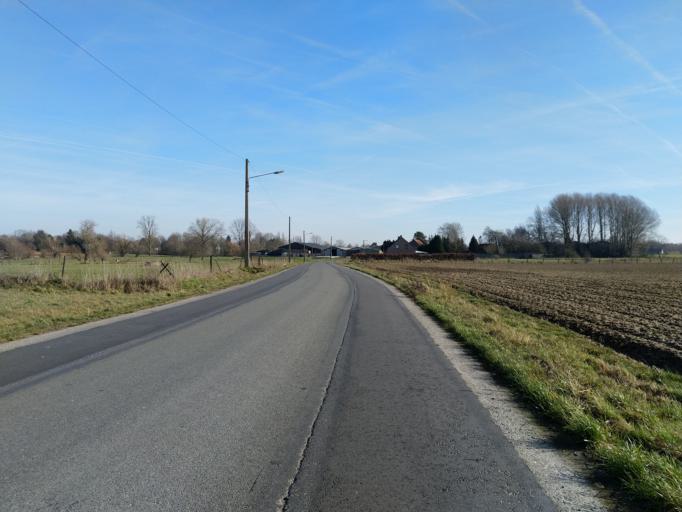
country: BE
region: Wallonia
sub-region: Province du Hainaut
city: Jurbise
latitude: 50.5303
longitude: 3.9323
